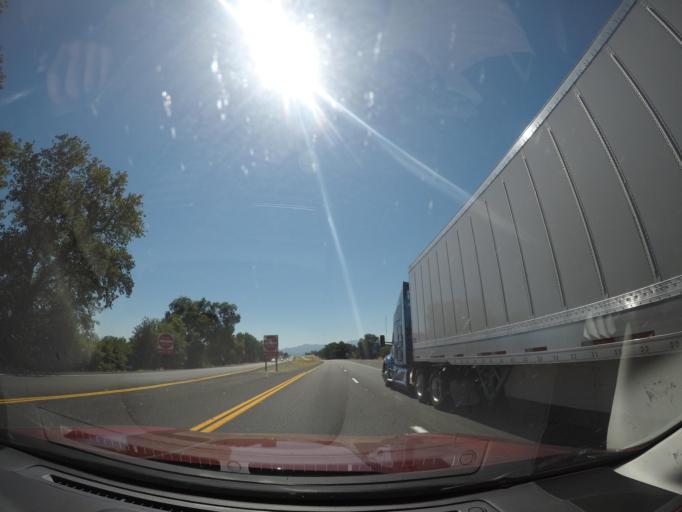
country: US
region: California
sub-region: Shasta County
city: Bella Vista
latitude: 40.6227
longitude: -122.3094
